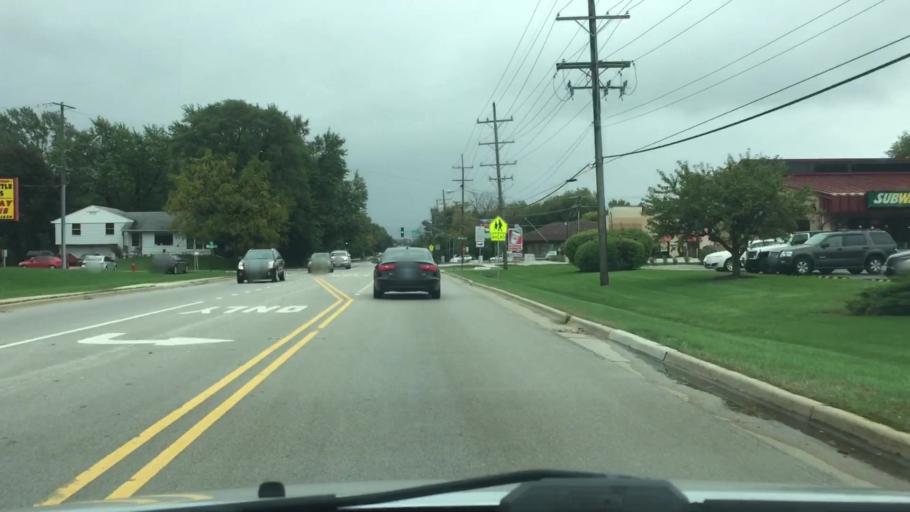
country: US
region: Illinois
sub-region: McHenry County
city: McHenry
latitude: 42.3377
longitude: -88.2746
